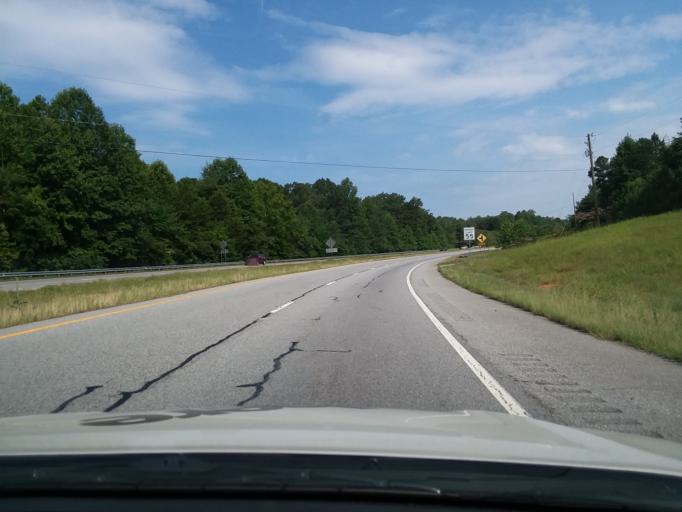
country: US
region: Georgia
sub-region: Rabun County
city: Clayton
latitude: 34.7788
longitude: -83.3988
